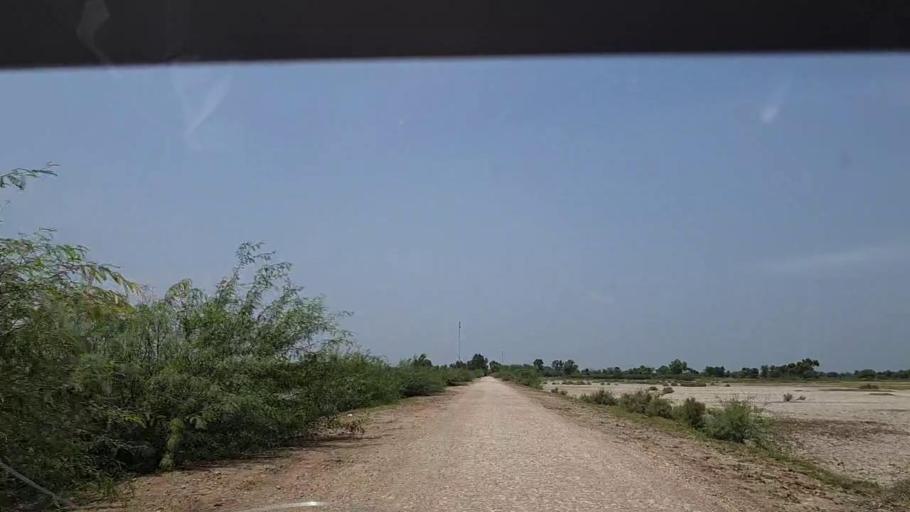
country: PK
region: Sindh
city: Adilpur
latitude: 27.9141
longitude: 69.2103
